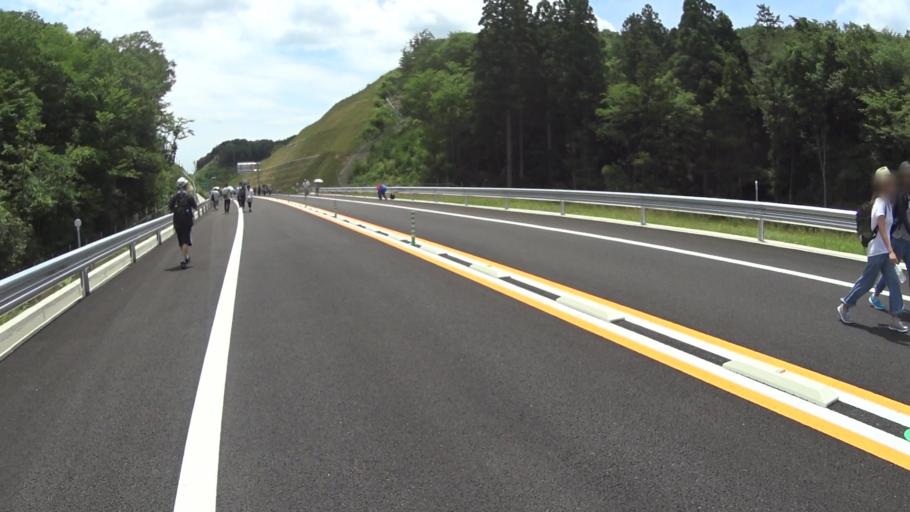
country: JP
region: Kyoto
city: Ayabe
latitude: 35.1687
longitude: 135.3744
